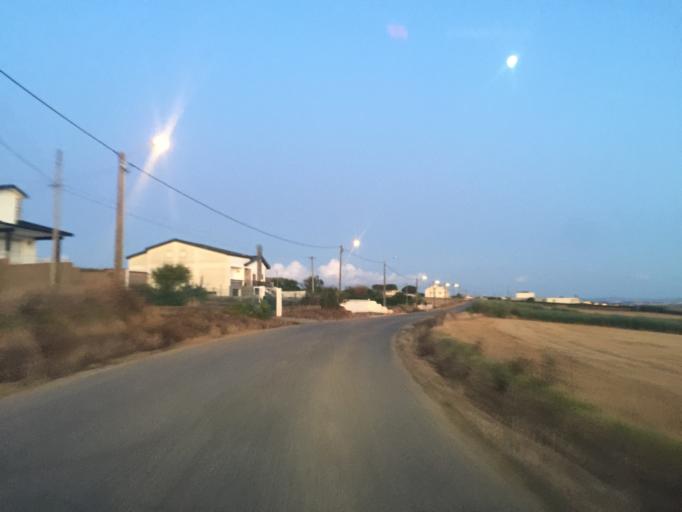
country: PT
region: Leiria
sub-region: Peniche
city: Atouguia da Baleia
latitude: 39.2921
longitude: -9.3091
